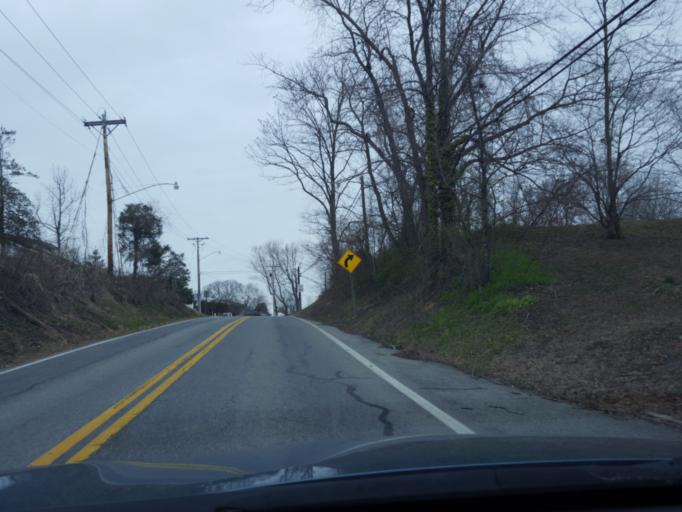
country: US
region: Maryland
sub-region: Calvert County
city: Prince Frederick
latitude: 38.5303
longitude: -76.5773
